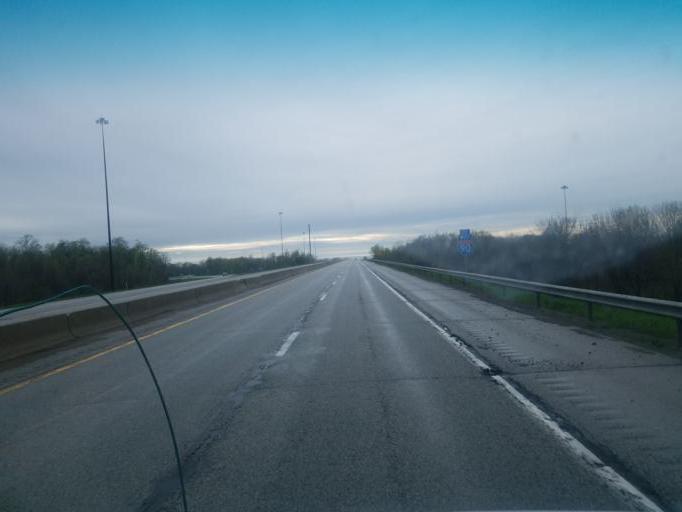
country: US
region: Pennsylvania
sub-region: Erie County
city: North East
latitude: 42.1533
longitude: -79.8886
